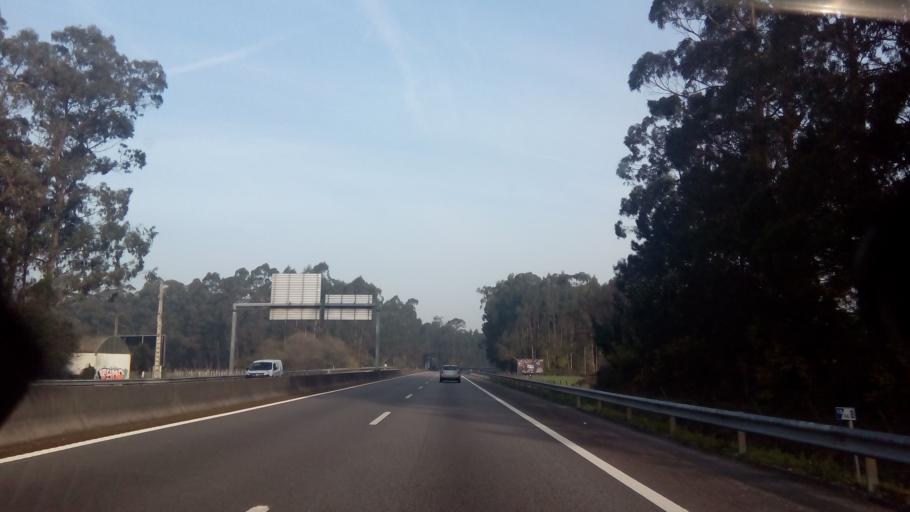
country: PT
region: Braga
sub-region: Esposende
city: Apulia
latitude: 41.4991
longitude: -8.7505
